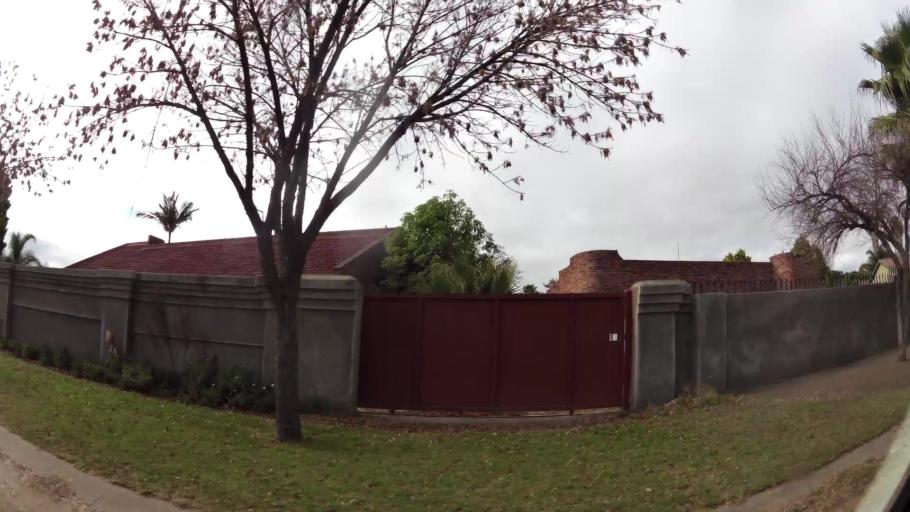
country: ZA
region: Limpopo
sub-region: Capricorn District Municipality
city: Polokwane
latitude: -23.9154
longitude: 29.4463
